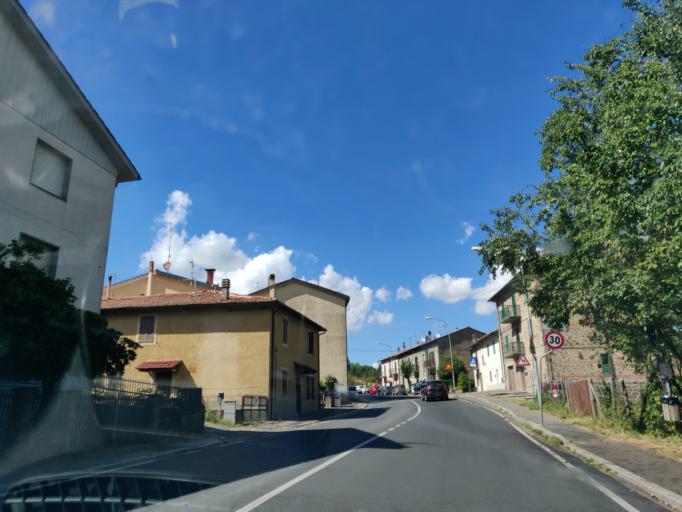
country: IT
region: Tuscany
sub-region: Provincia di Siena
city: Abbadia San Salvatore
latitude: 42.8881
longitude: 11.6669
